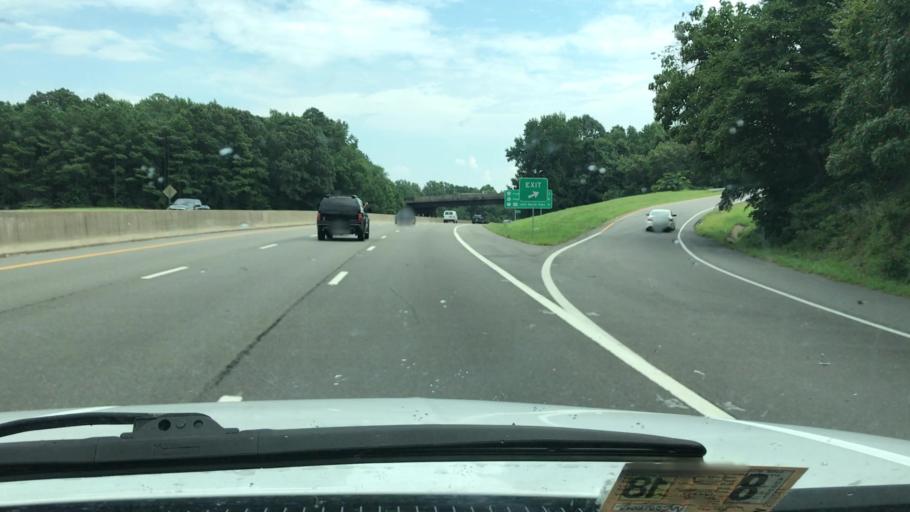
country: US
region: Virginia
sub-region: Chesterfield County
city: Bensley
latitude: 37.4633
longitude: -77.5001
